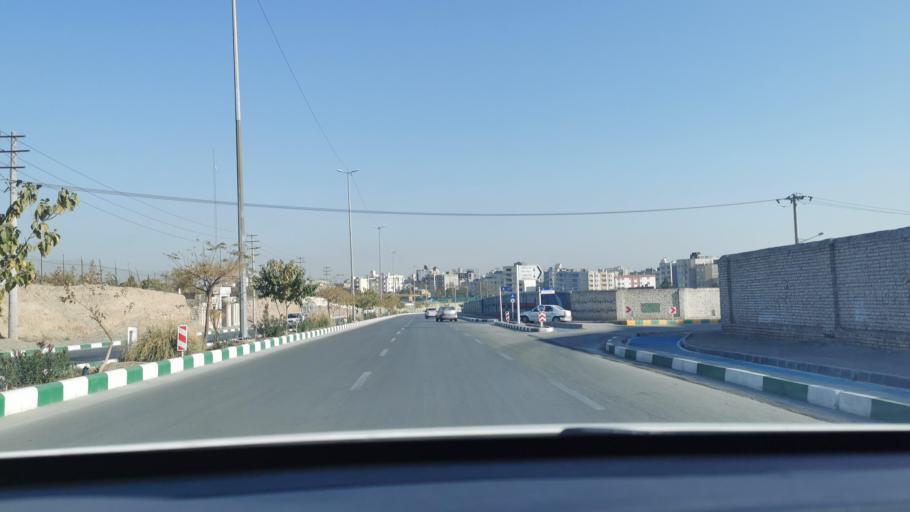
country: IR
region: Razavi Khorasan
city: Mashhad
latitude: 36.2796
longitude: 59.5415
